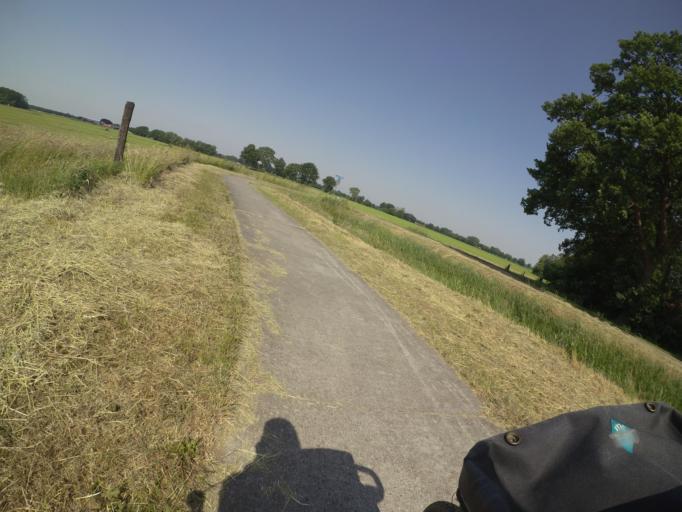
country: NL
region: Drenthe
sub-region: Gemeente De Wolden
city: Ruinen
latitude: 52.6862
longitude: 6.3130
